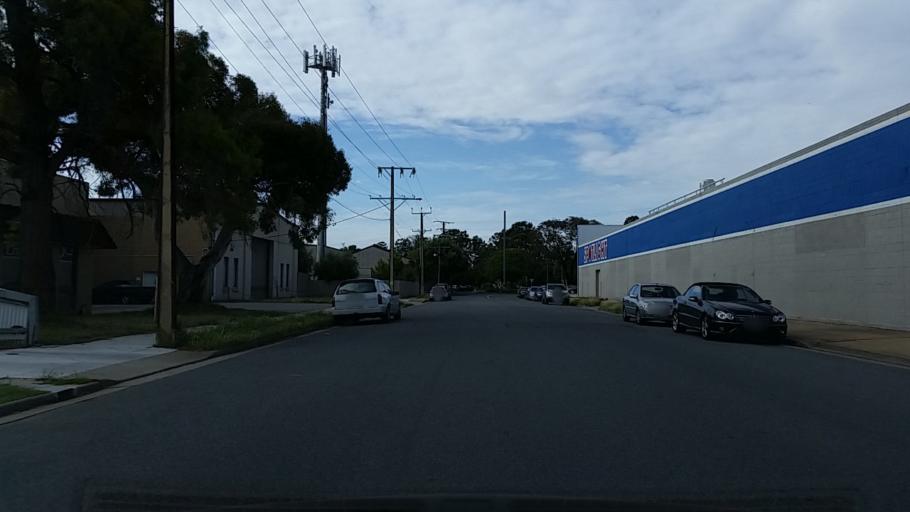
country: AU
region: South Australia
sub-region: Charles Sturt
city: Albert Park
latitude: -34.8759
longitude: 138.5253
